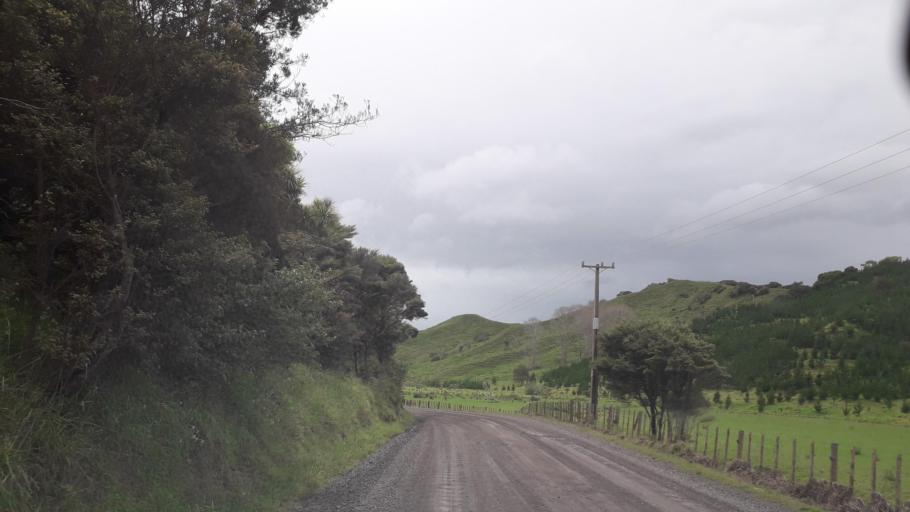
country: NZ
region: Northland
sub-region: Far North District
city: Ahipara
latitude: -35.4276
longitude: 173.3541
